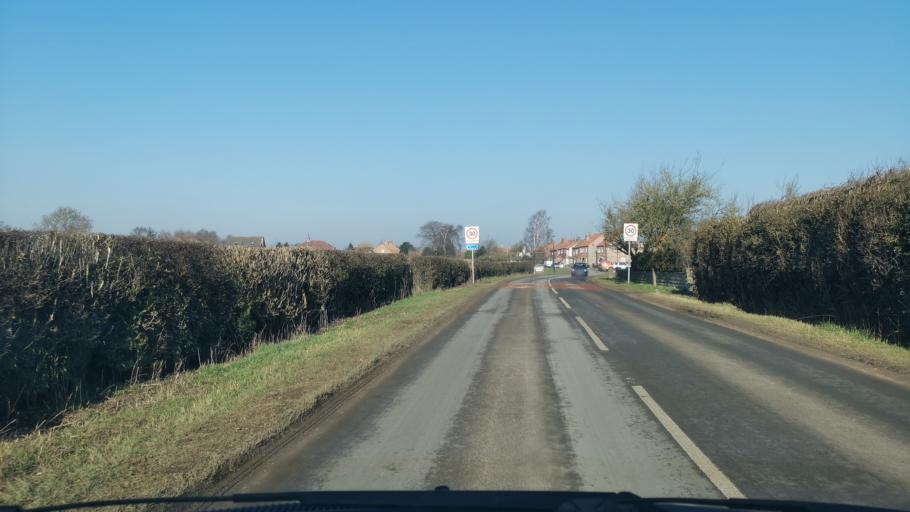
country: GB
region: England
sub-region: City of York
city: Murton
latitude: 53.9643
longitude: -1.0099
